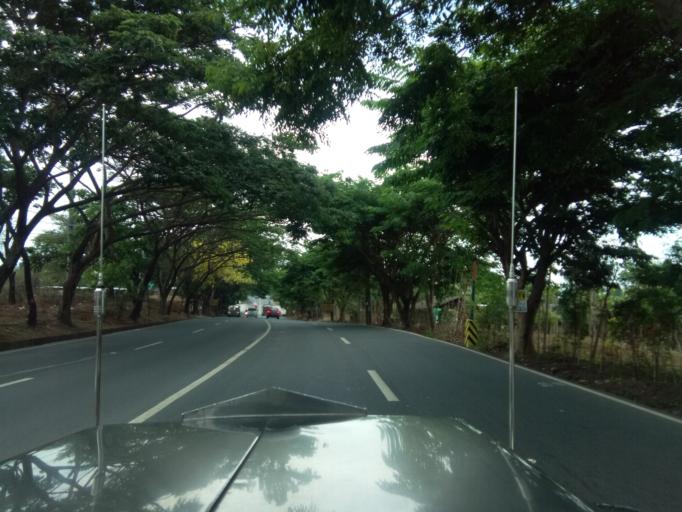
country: PH
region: Calabarzon
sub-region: Province of Cavite
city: Aliang
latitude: 14.2837
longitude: 120.8933
